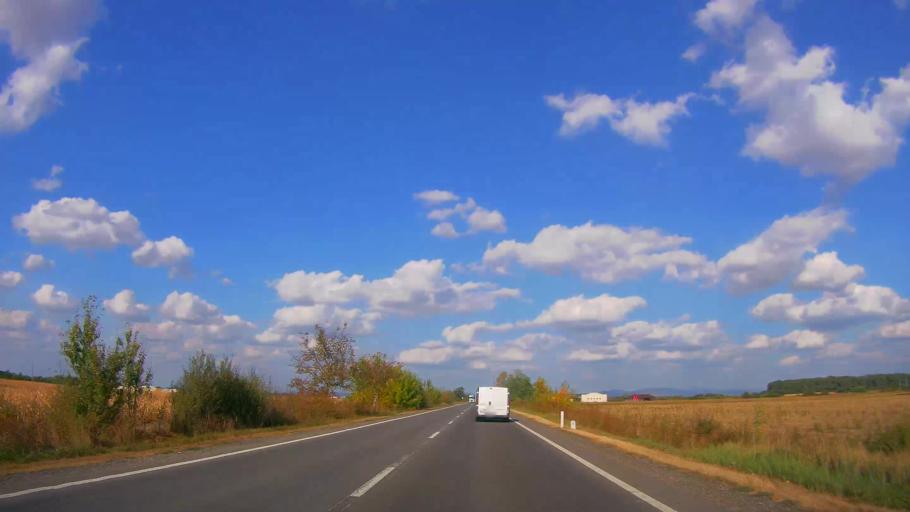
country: RO
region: Satu Mare
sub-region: Comuna Agris
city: Agris
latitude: 47.8561
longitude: 22.9801
